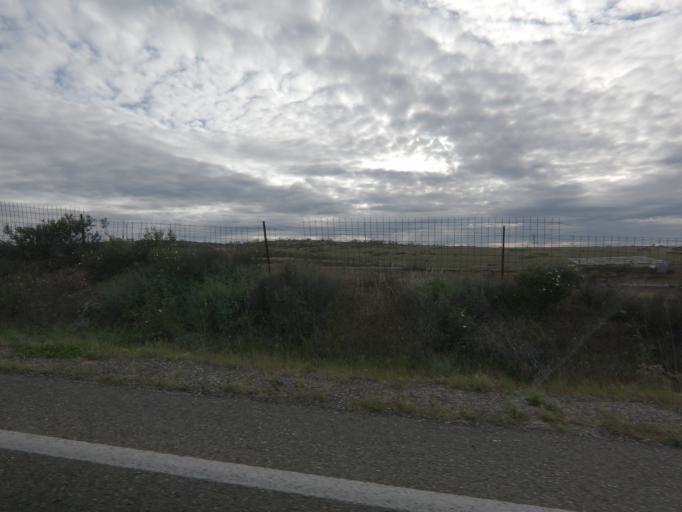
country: ES
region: Extremadura
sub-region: Provincia de Caceres
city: Torrejoncillo
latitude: 39.9340
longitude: -6.5056
